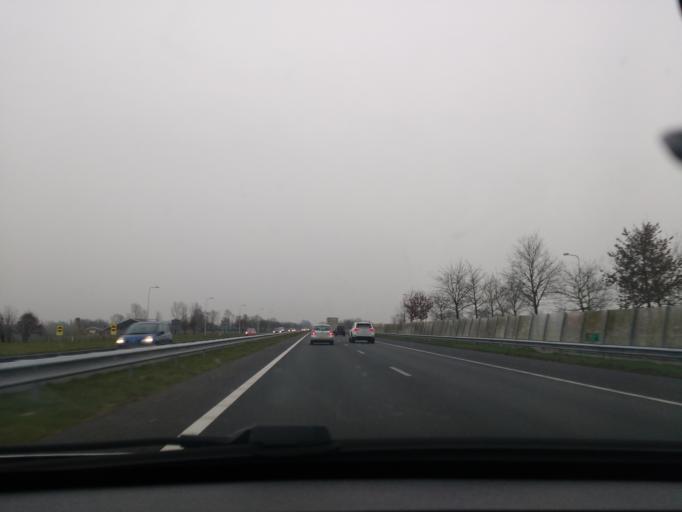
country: NL
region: Gelderland
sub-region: Gemeente Ede
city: Lunteren
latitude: 52.0634
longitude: 5.6107
